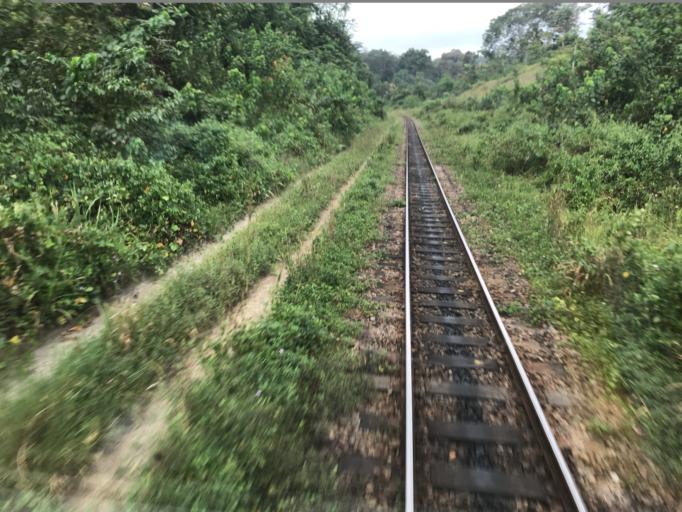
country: CM
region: Centre
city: Eseka
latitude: 3.5940
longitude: 10.8314
